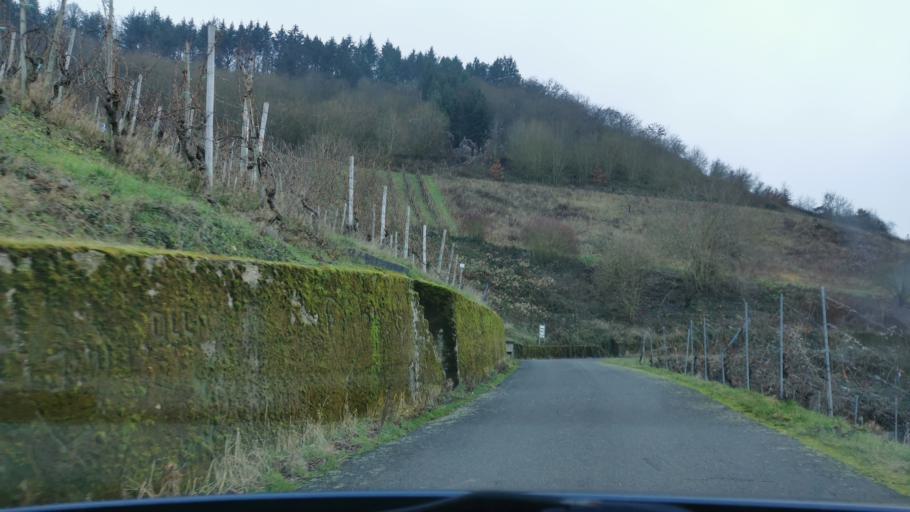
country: DE
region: Rheinland-Pfalz
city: Wintrich
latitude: 49.8738
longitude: 6.9523
